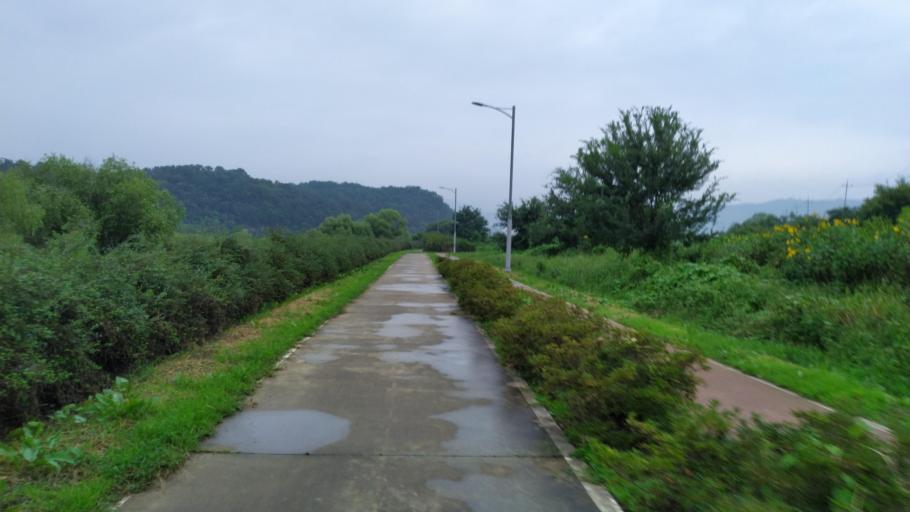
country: KR
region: Daegu
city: Daegu
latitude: 35.9030
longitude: 128.6287
